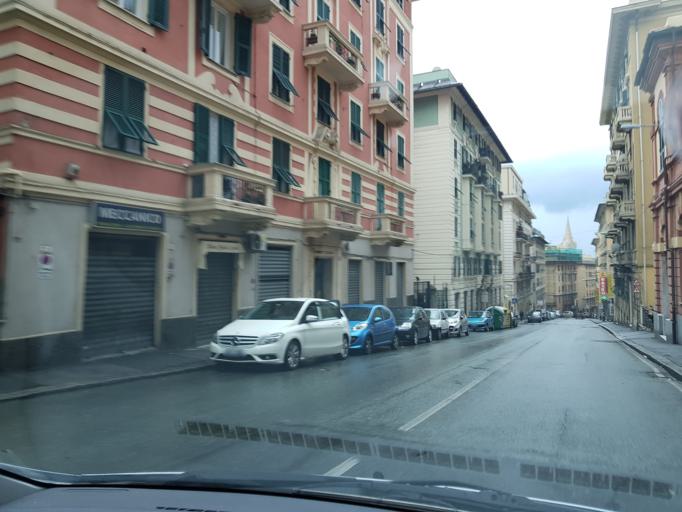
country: IT
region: Liguria
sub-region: Provincia di Genova
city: San Teodoro
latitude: 44.4167
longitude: 8.9102
